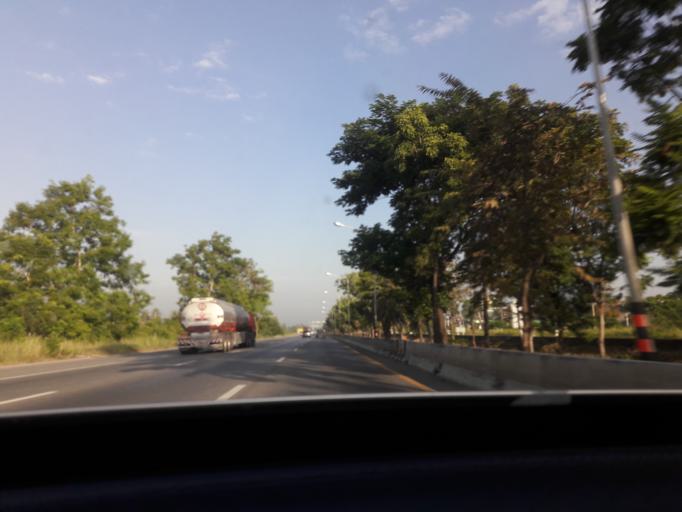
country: TH
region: Ang Thong
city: Chaiyo
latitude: 14.6845
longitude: 100.4644
